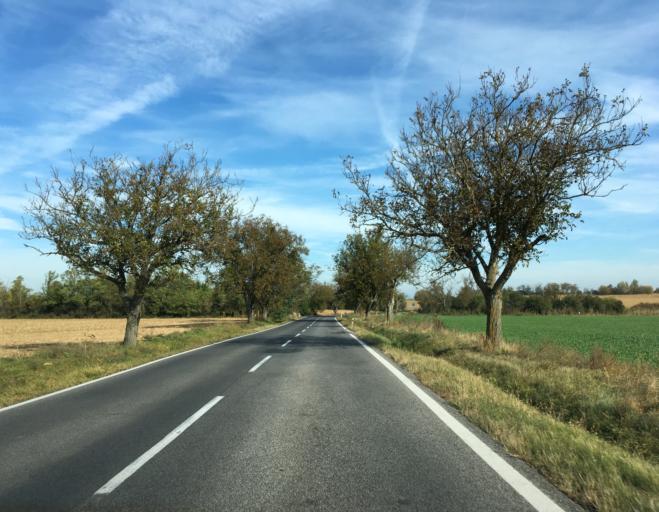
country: SK
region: Nitriansky
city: Zeliezovce
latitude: 48.0762
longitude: 18.5287
